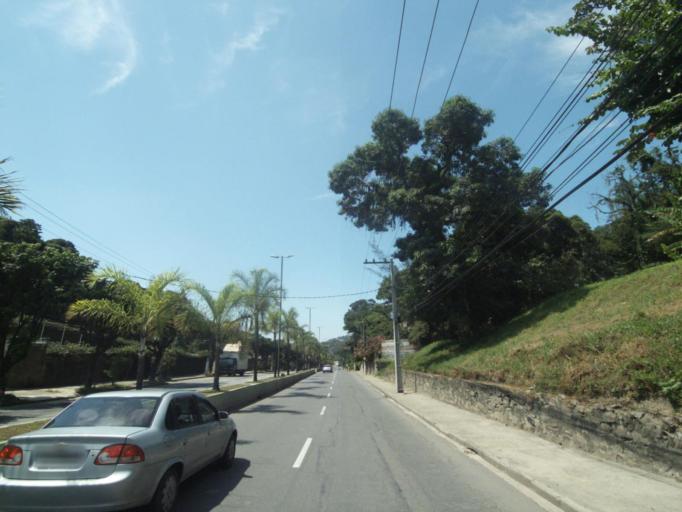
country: BR
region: Rio de Janeiro
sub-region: Niteroi
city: Niteroi
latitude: -22.9034
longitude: -43.0464
